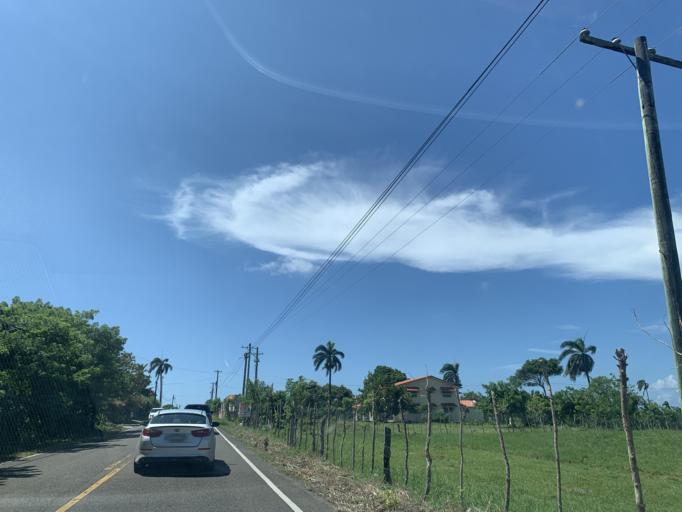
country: DO
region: Maria Trinidad Sanchez
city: Cabrera
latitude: 19.6690
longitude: -69.9518
